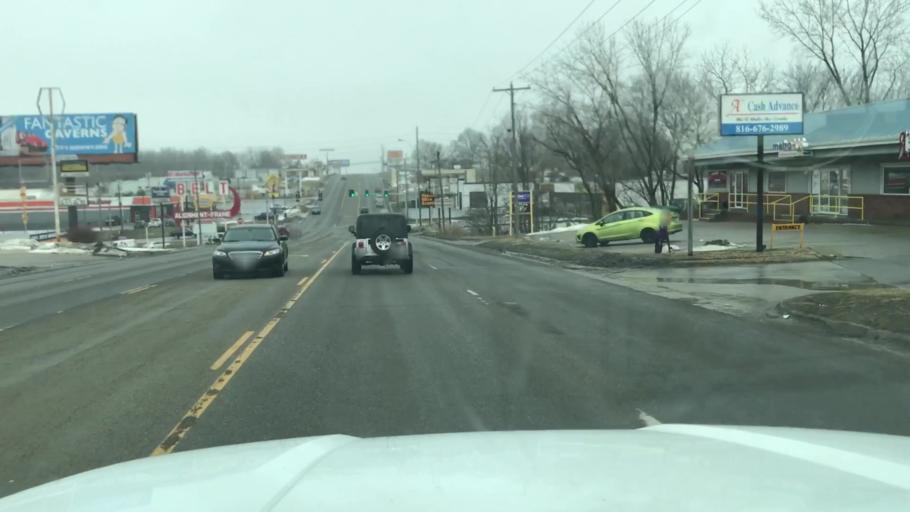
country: US
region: Missouri
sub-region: Buchanan County
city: Saint Joseph
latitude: 39.7612
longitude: -94.8036
